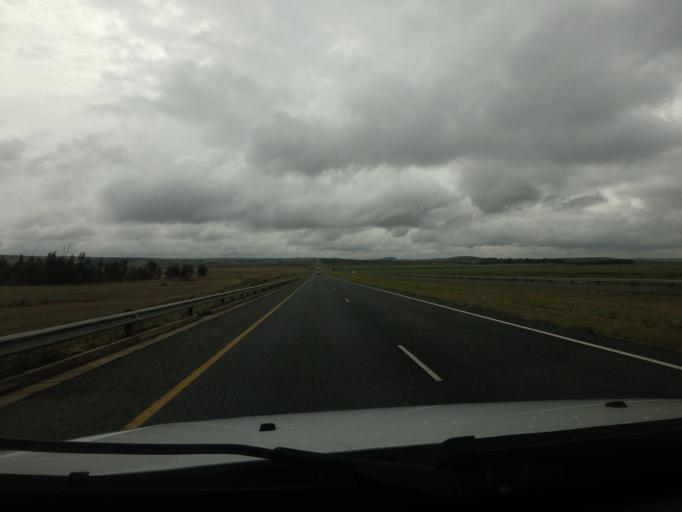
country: ZA
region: Mpumalanga
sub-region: Nkangala District Municipality
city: Witbank
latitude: -25.8696
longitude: 29.0009
